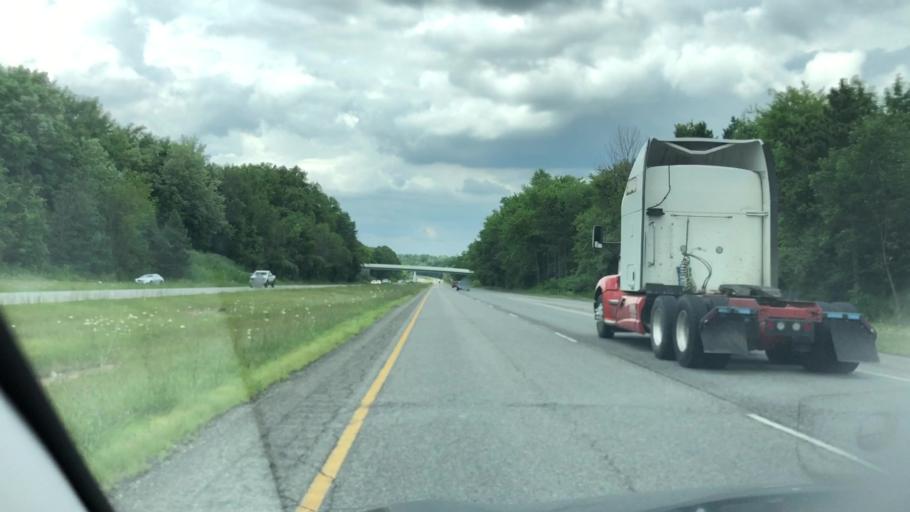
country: US
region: Ohio
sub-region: Summit County
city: Norton
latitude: 41.0517
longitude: -81.6620
